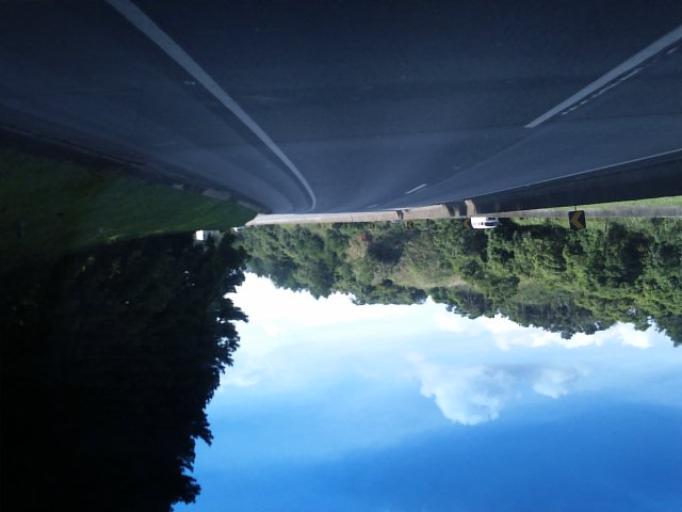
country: BR
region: Parana
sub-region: Campina Grande Do Sul
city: Campina Grande do Sul
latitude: -25.2060
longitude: -48.8955
